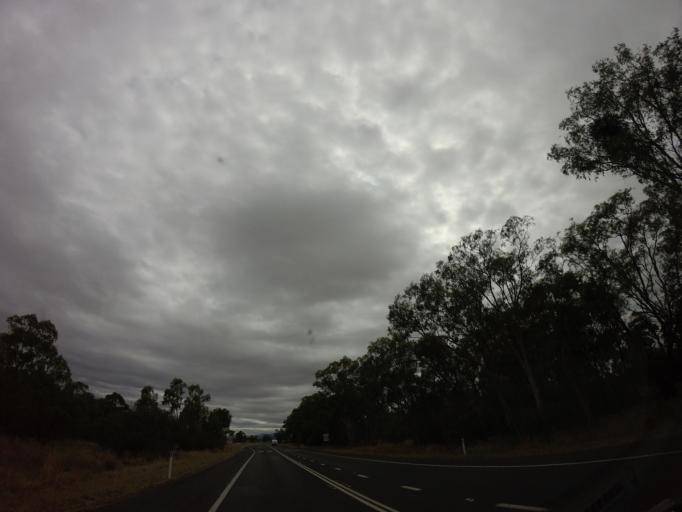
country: AU
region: New South Wales
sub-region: Narrabri
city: Narrabri
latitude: -30.3506
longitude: 149.7548
